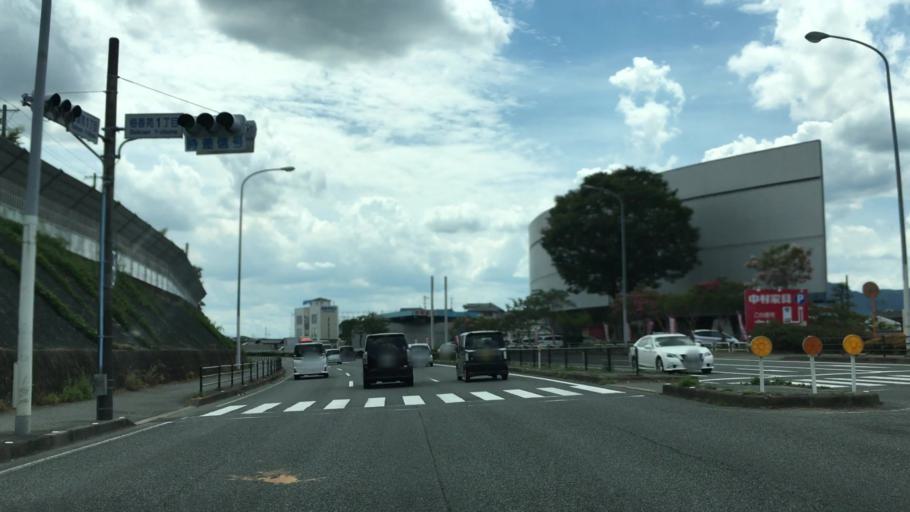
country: JP
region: Fukuoka
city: Dazaifu
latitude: 33.5000
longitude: 130.5314
